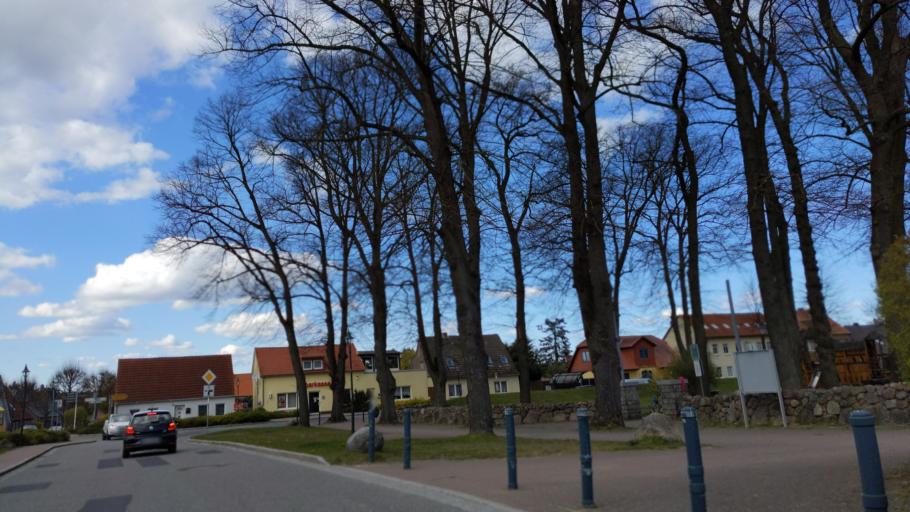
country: DE
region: Mecklenburg-Vorpommern
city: Selmsdorf
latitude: 53.8816
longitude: 10.8599
